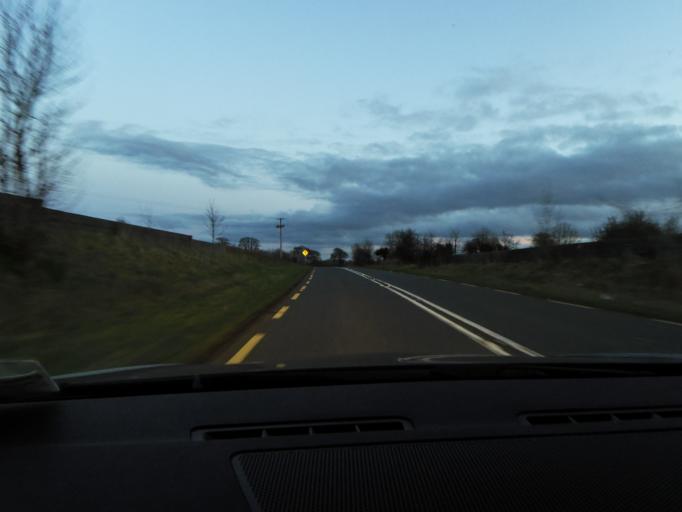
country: IE
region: Connaught
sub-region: Roscommon
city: Boyle
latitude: 53.8156
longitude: -8.2278
